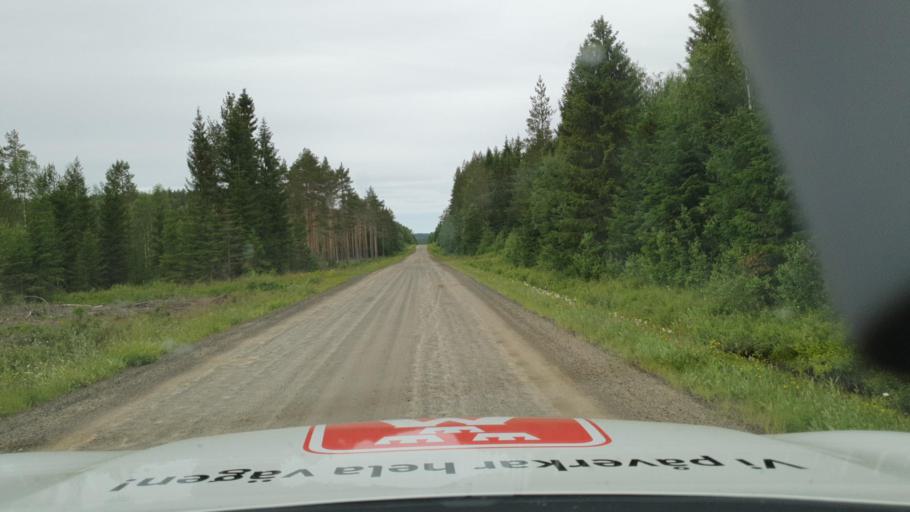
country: SE
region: Vaesterbotten
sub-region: Skelleftea Kommun
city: Burtraesk
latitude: 64.3250
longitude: 20.6329
